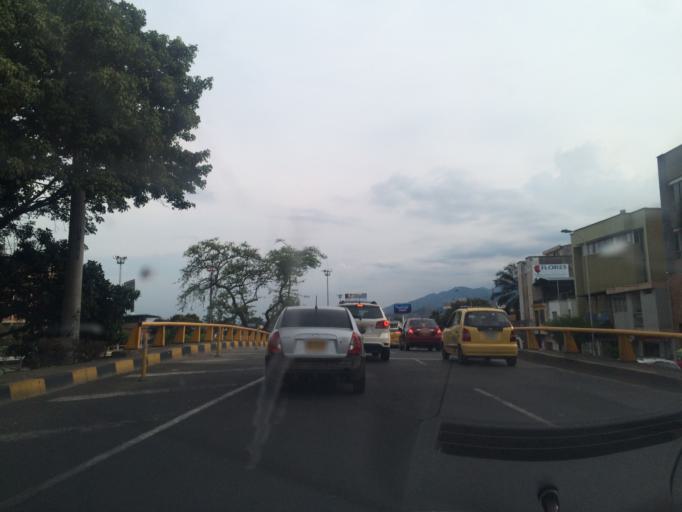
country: CO
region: Valle del Cauca
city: Cali
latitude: 3.4411
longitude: -76.5368
